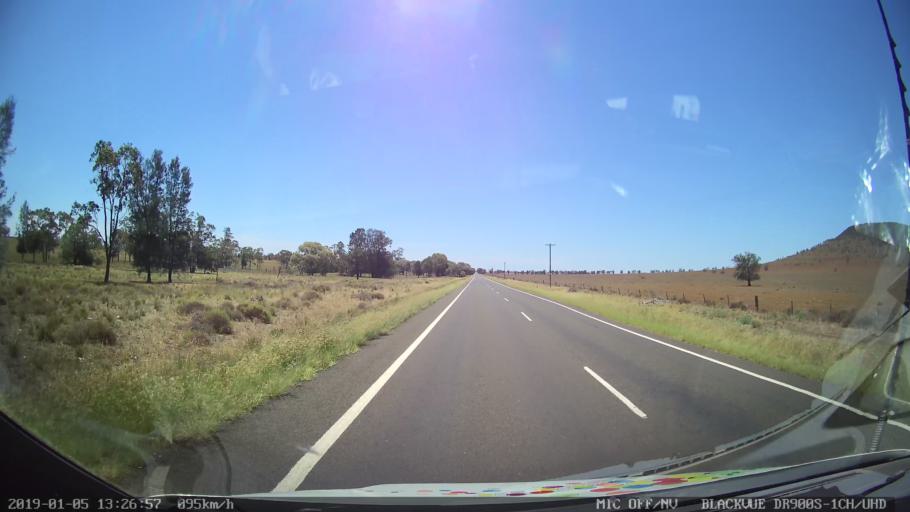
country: AU
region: New South Wales
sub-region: Gunnedah
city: Gunnedah
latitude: -31.0487
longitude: 150.0226
